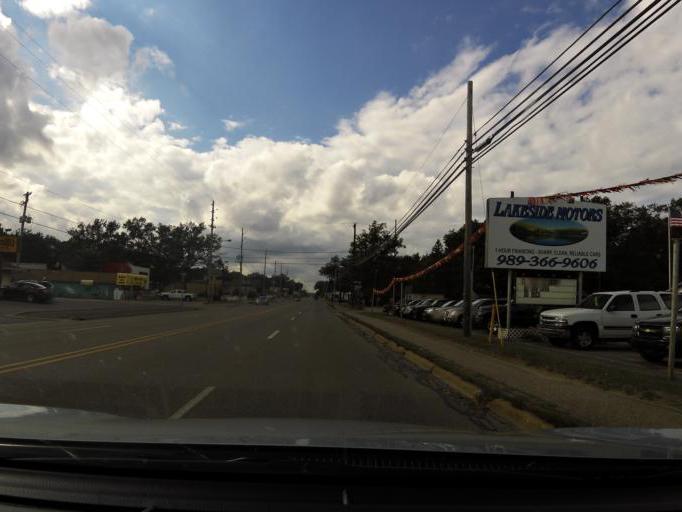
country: US
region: Michigan
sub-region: Roscommon County
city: Prudenville
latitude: 44.2987
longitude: -84.6965
